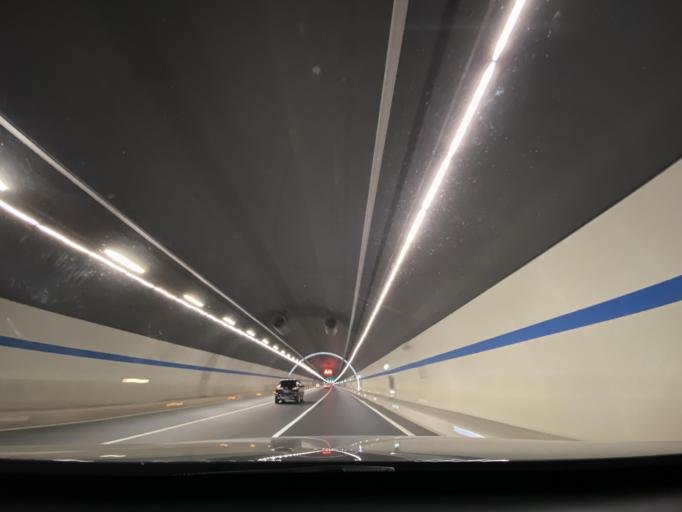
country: CN
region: Sichuan
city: Longquan
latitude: 30.4426
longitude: 104.2442
